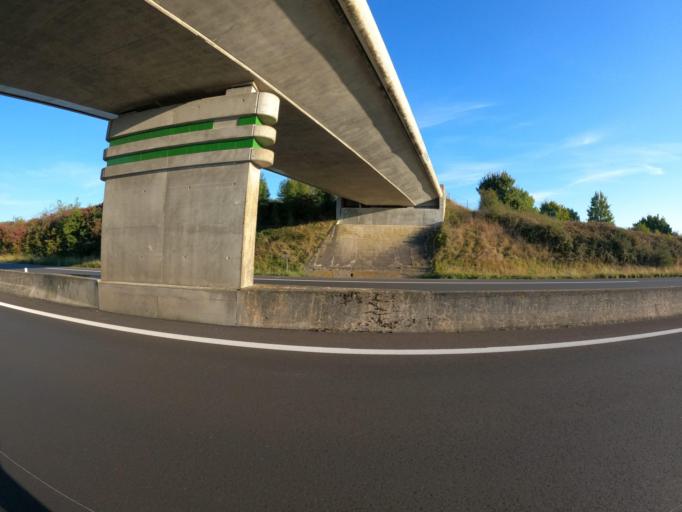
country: FR
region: Pays de la Loire
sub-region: Departement de la Vendee
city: Beaurepaire
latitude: 46.8929
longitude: -1.0924
